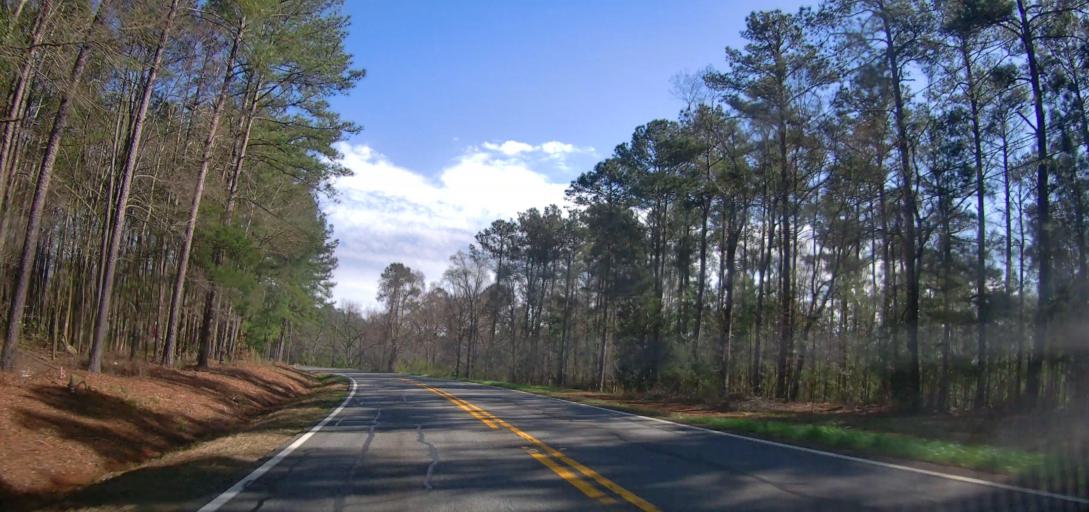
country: US
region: Georgia
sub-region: Butts County
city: Indian Springs
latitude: 33.1489
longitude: -83.9534
